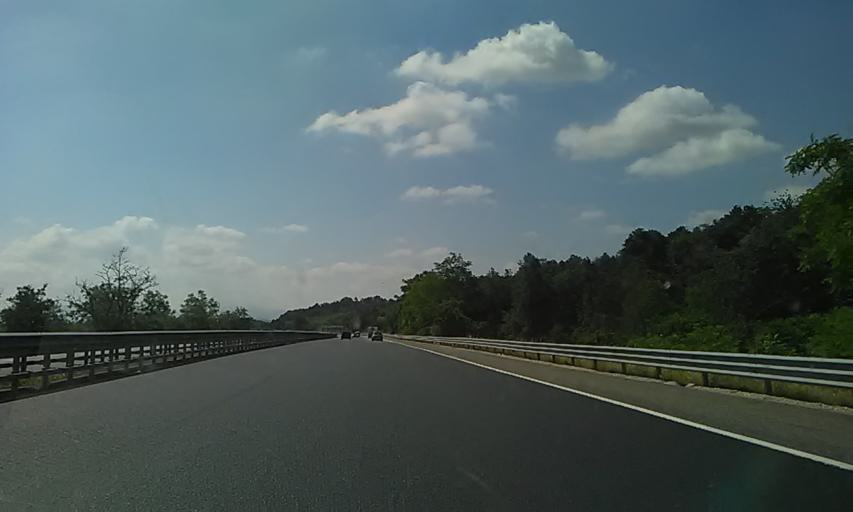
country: IT
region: Piedmont
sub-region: Provincia di Alessandria
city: Predosa
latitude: 44.7453
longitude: 8.6486
